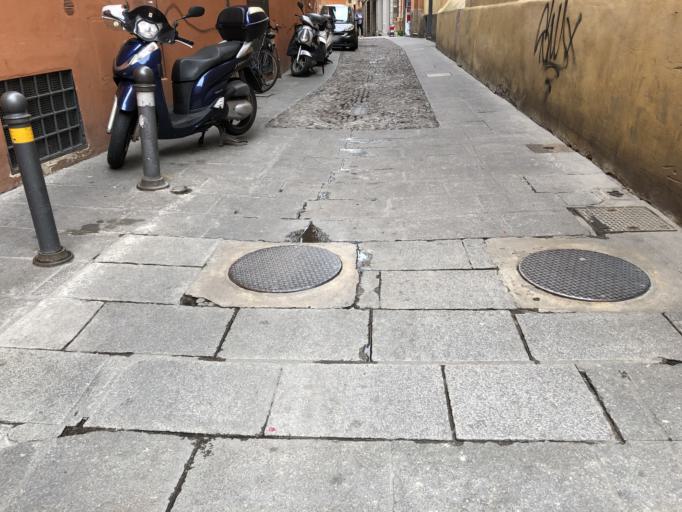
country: IT
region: Emilia-Romagna
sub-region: Provincia di Bologna
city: Bologna
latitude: 44.4952
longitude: 11.3475
